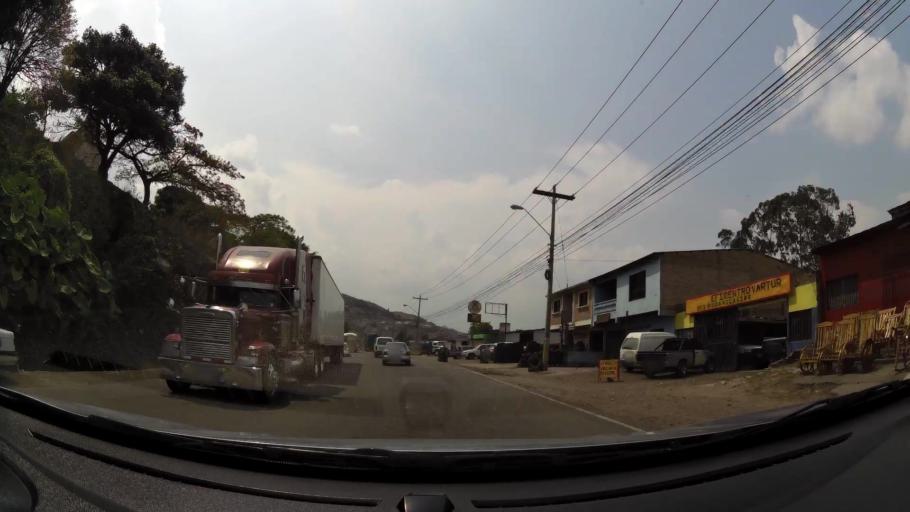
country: HN
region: Francisco Morazan
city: Tegucigalpa
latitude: 14.1181
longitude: -87.2233
